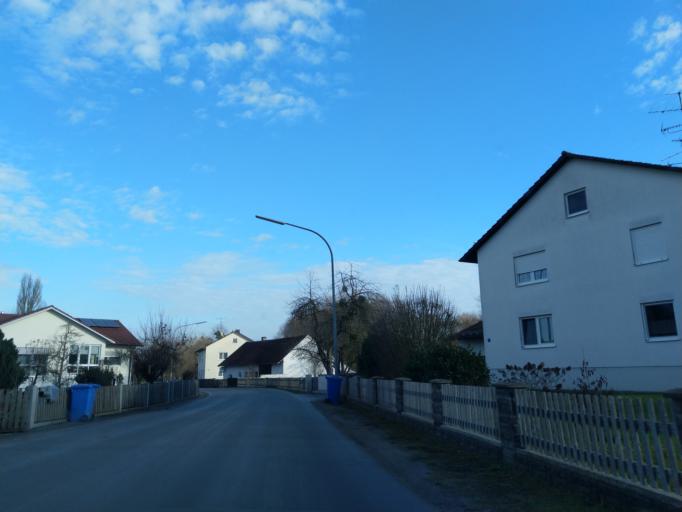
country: DE
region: Bavaria
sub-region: Lower Bavaria
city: Osterhofen
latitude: 48.7303
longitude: 13.0170
